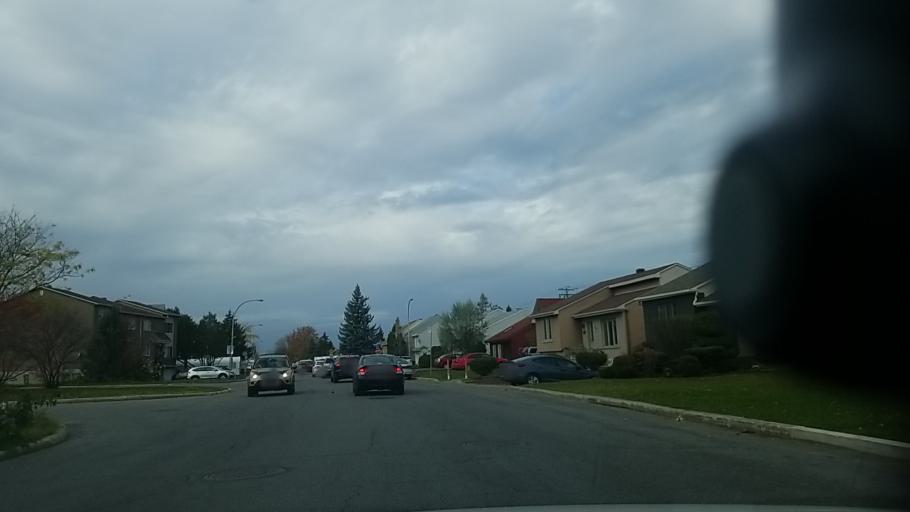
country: CA
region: Quebec
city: Dollard-Des Ormeaux
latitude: 45.5333
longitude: -73.7811
